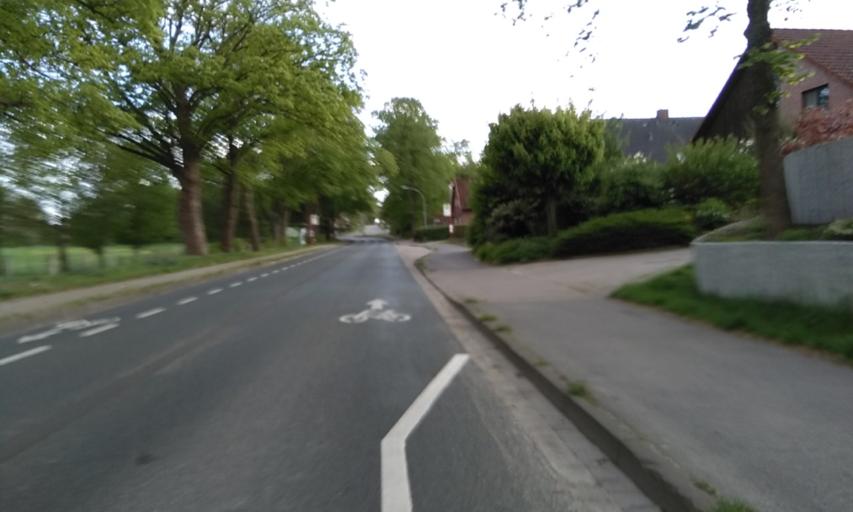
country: DE
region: Lower Saxony
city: Buxtehude
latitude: 53.4521
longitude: 9.6646
